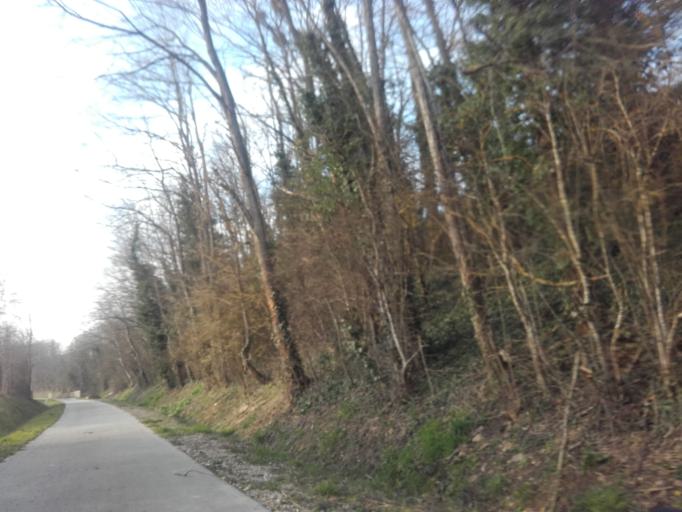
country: FR
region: Bourgogne
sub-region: Departement de la Cote-d'Or
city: Nolay
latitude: 46.9055
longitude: 4.6614
